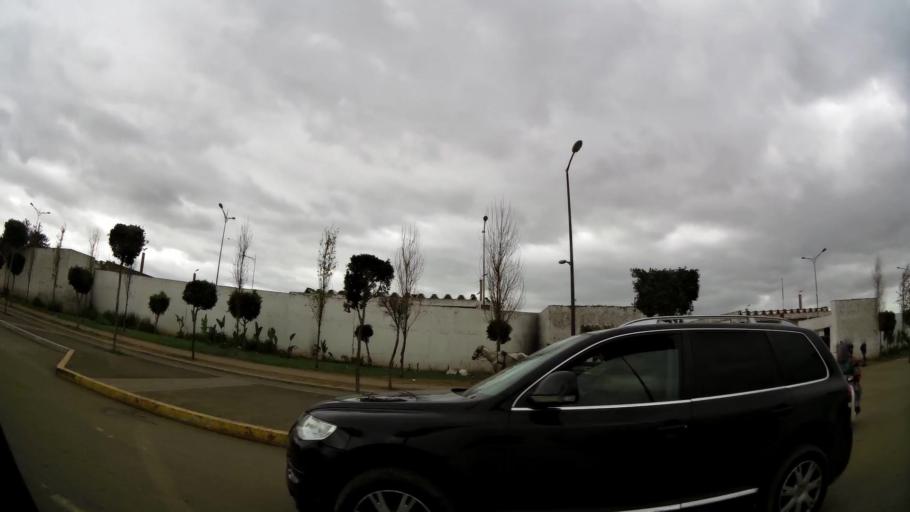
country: MA
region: Grand Casablanca
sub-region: Casablanca
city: Casablanca
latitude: 33.5550
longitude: -7.5565
